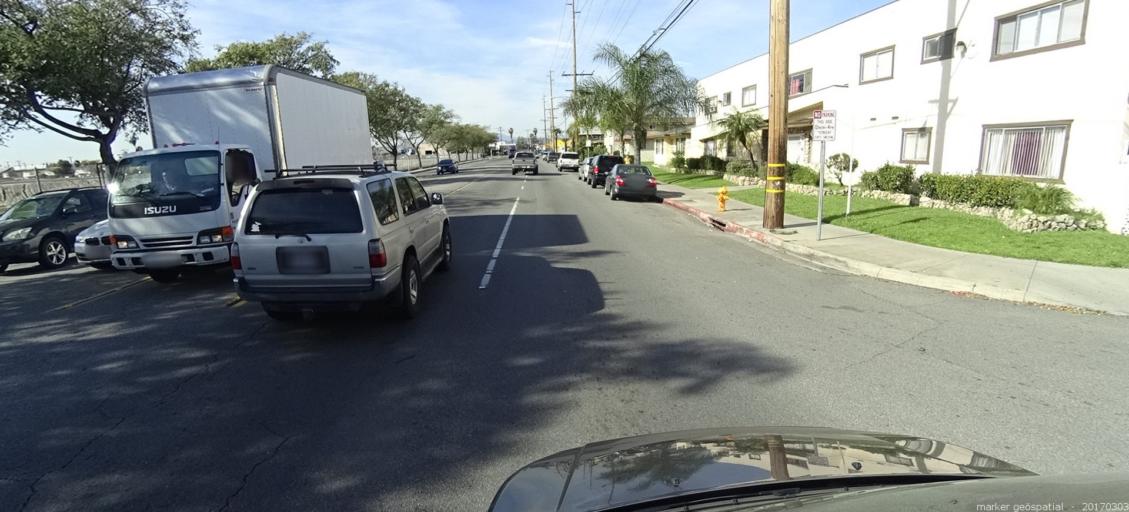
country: US
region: California
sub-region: Orange County
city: Anaheim
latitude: 33.8482
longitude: -117.9060
